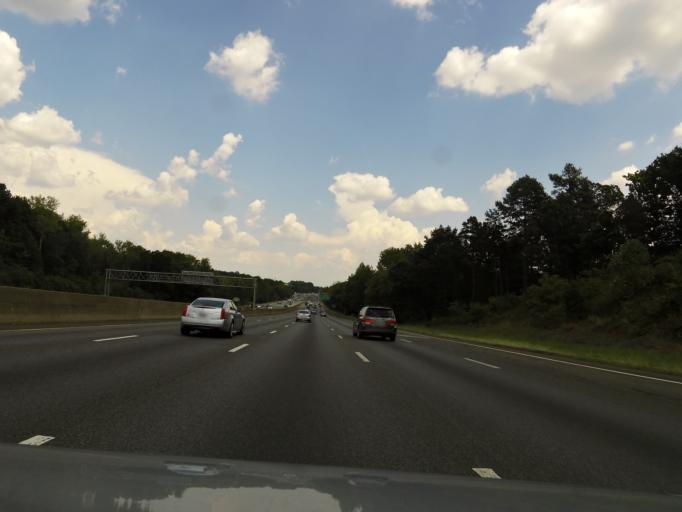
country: US
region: North Carolina
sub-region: Gaston County
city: Belmont
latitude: 35.2573
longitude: -81.0197
